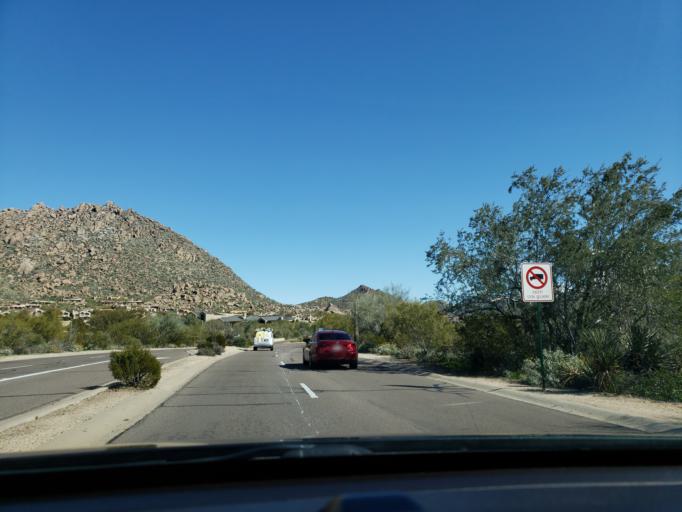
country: US
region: Arizona
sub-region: Maricopa County
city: Carefree
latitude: 33.7126
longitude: -111.8566
